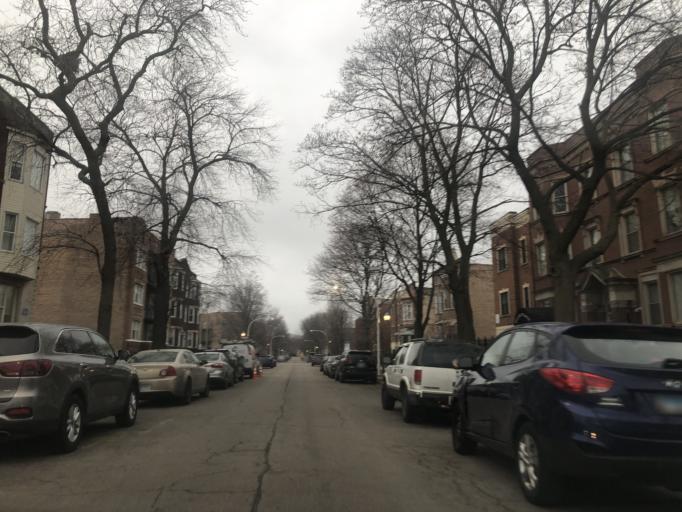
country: US
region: Illinois
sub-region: Cook County
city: Chicago
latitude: 41.7771
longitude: -87.6004
